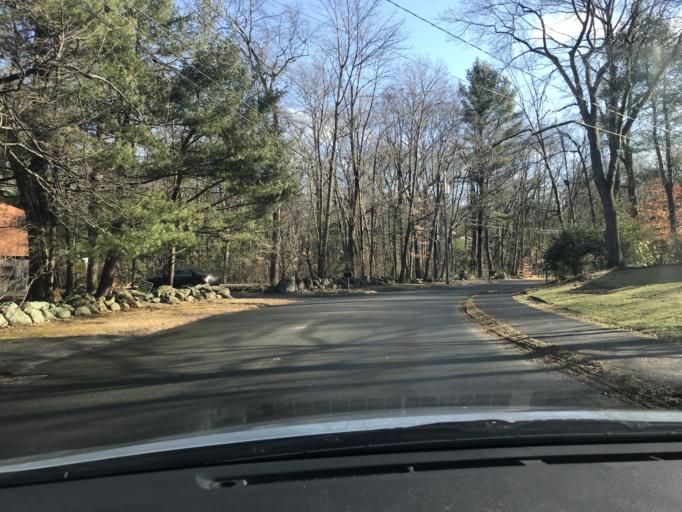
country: US
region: Massachusetts
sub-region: Middlesex County
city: Lexington
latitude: 42.4800
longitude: -71.2307
